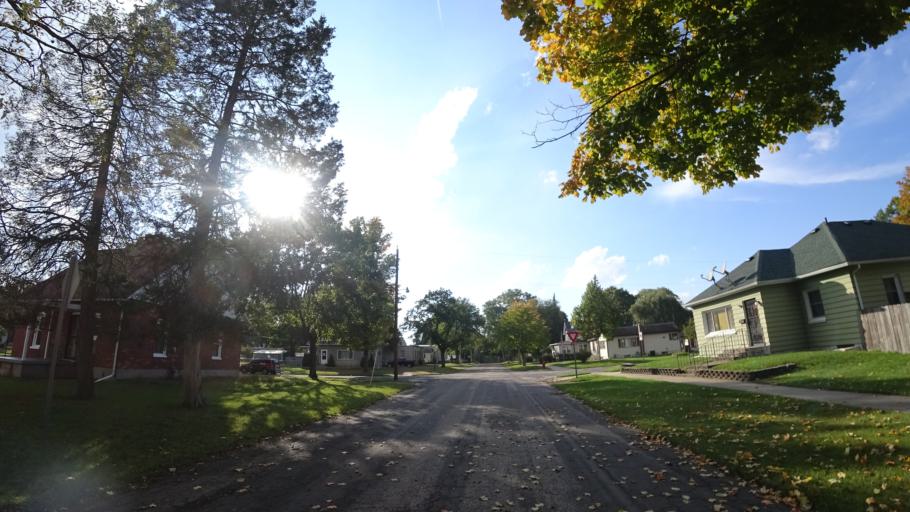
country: US
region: Michigan
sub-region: Saint Joseph County
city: Three Rivers
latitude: 41.9483
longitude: -85.6223
